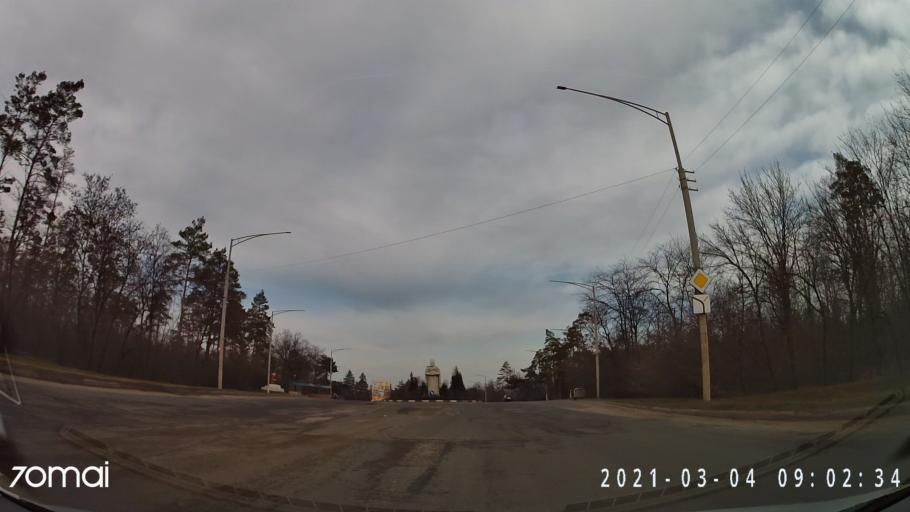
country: MD
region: Balti
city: Balti
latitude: 47.7441
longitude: 27.9536
